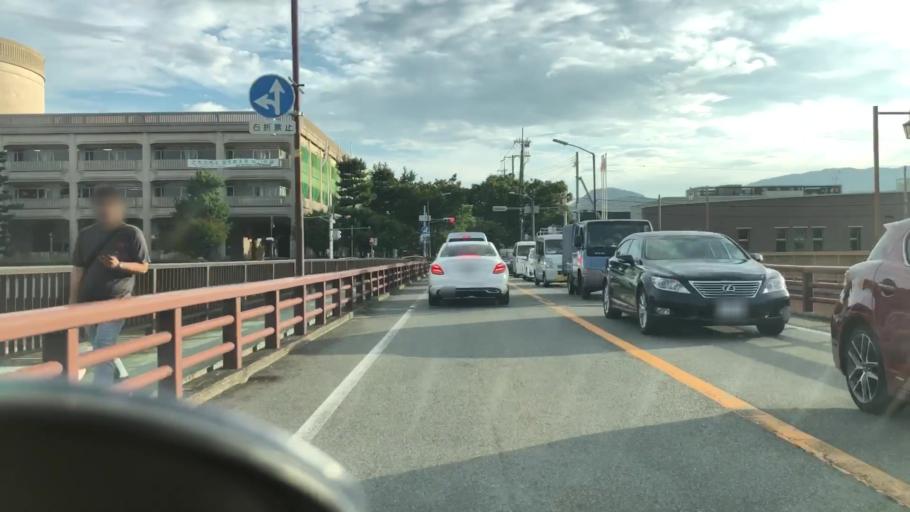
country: JP
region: Hyogo
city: Takarazuka
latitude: 34.8010
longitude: 135.3607
